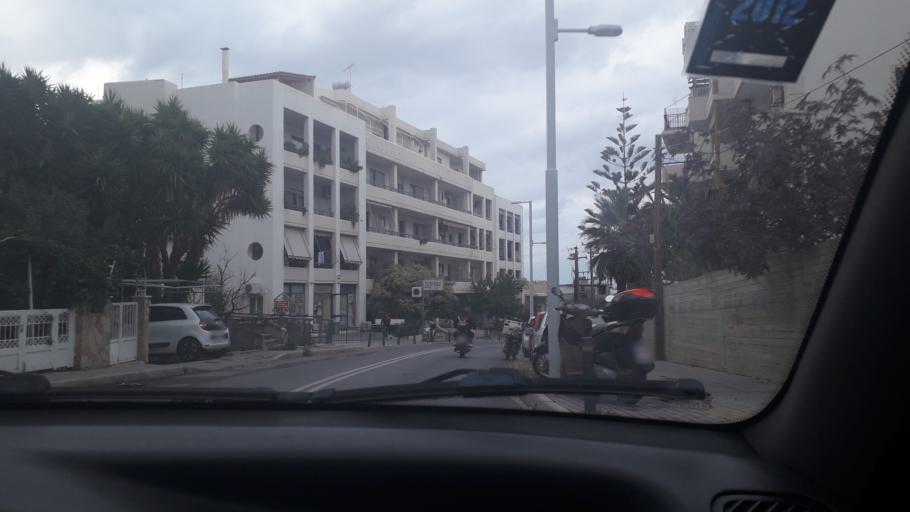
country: GR
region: Crete
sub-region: Nomos Rethymnis
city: Rethymno
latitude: 35.3615
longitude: 24.4732
